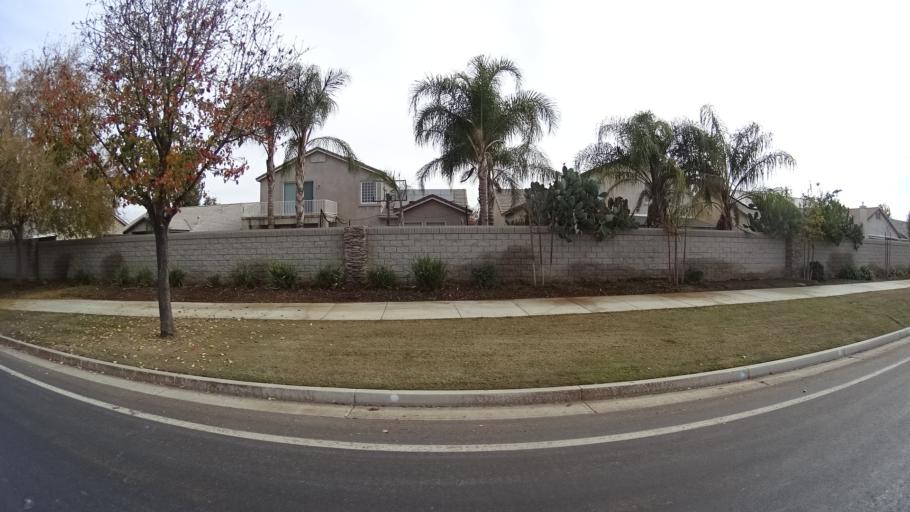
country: US
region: California
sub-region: Kern County
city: Rosedale
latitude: 35.4239
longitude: -119.1276
